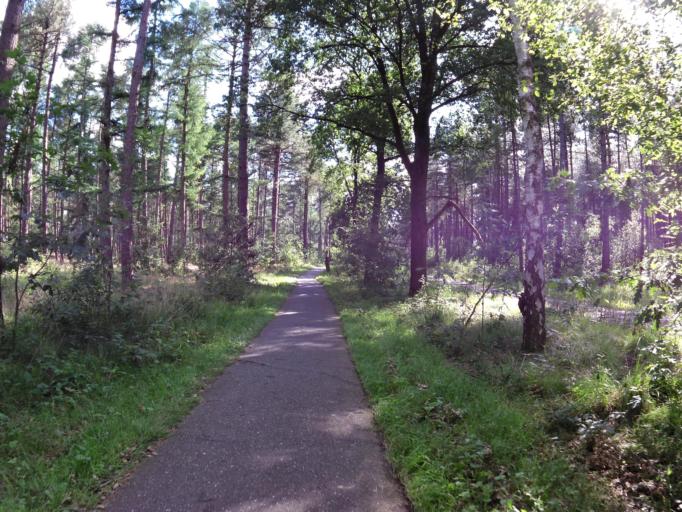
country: NL
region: North Brabant
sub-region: Gemeente Geldrop-Mierlo
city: Geldrop
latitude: 51.3998
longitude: 5.5246
